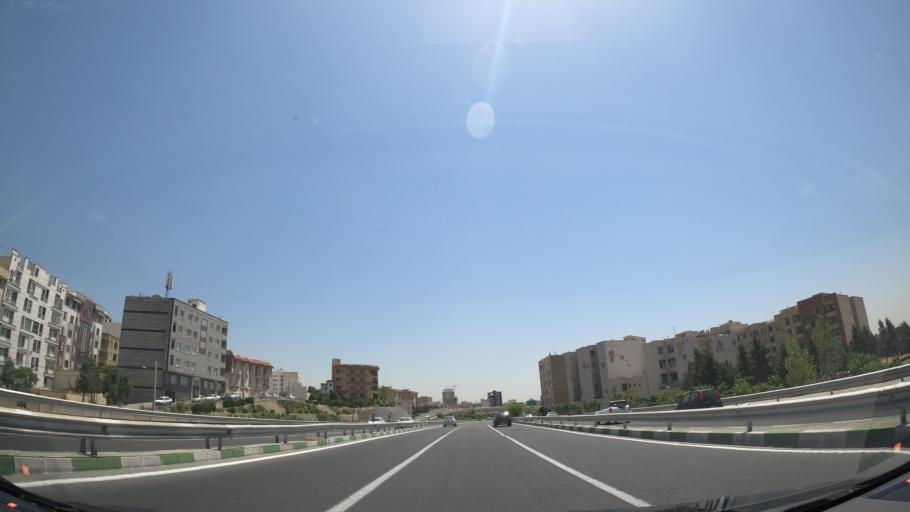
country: IR
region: Tehran
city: Tajrish
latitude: 35.7704
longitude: 51.3197
